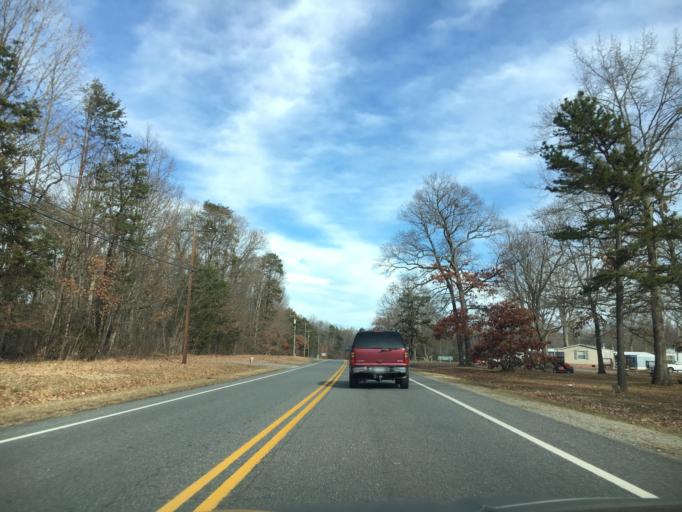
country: US
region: Virginia
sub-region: Louisa County
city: Louisa
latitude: 38.0200
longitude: -77.9027
